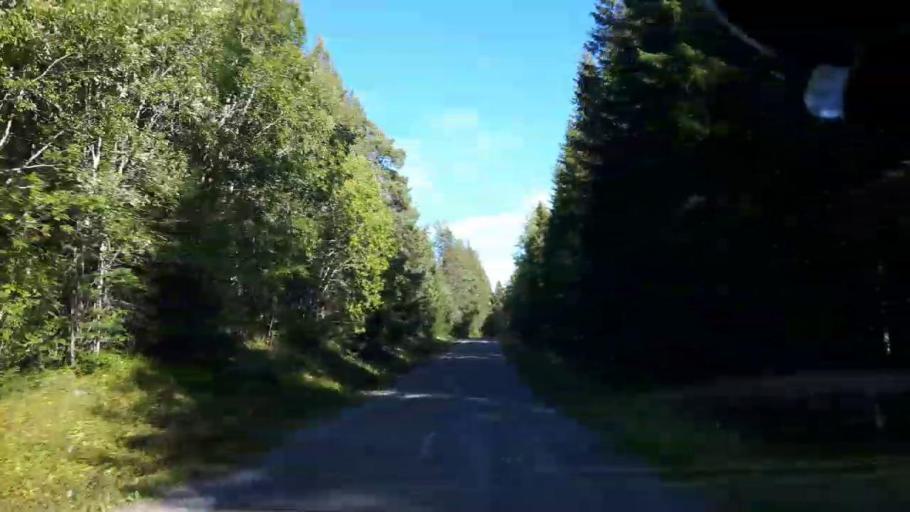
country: SE
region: Jaemtland
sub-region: Ragunda Kommun
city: Hammarstrand
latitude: 63.5283
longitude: 16.0683
